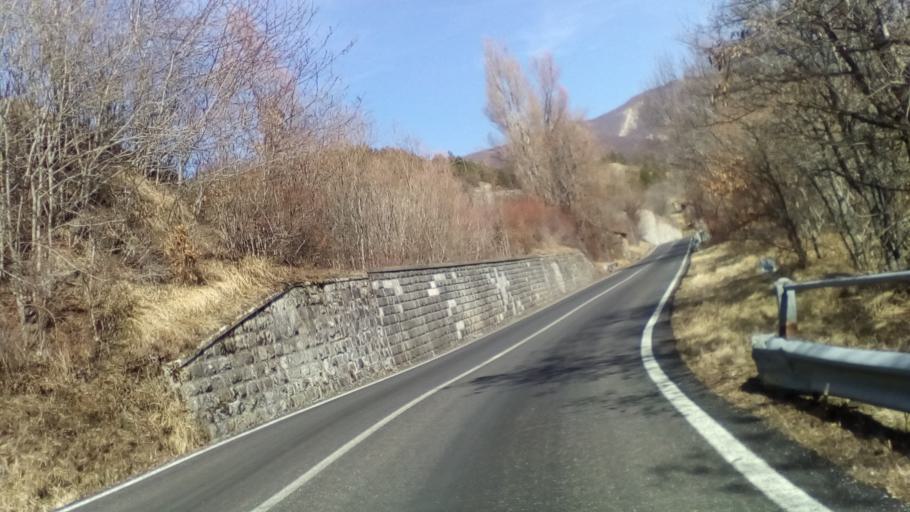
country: IT
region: Emilia-Romagna
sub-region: Provincia di Modena
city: Riolunato
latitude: 44.2447
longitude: 10.6329
